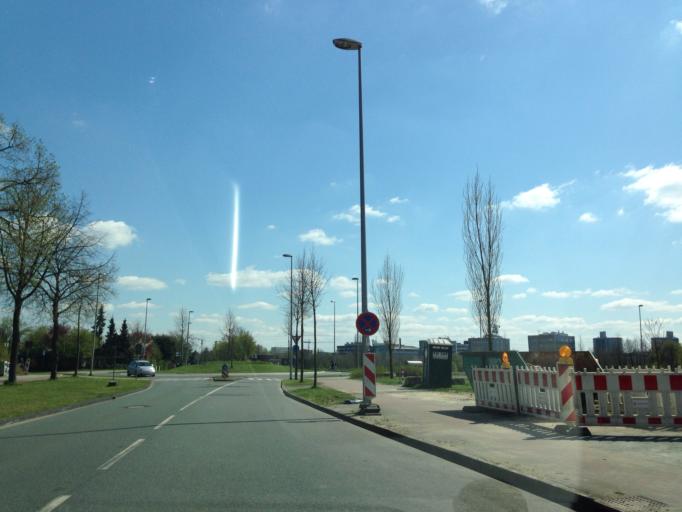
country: DE
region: North Rhine-Westphalia
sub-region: Regierungsbezirk Munster
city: Muenster
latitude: 51.9741
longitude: 7.5894
